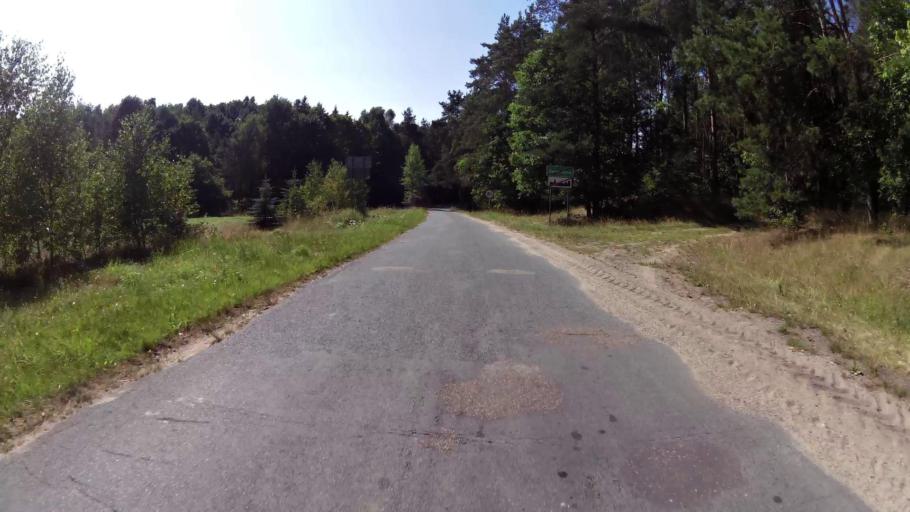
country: PL
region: West Pomeranian Voivodeship
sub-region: Powiat drawski
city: Czaplinek
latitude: 53.4324
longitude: 16.2673
